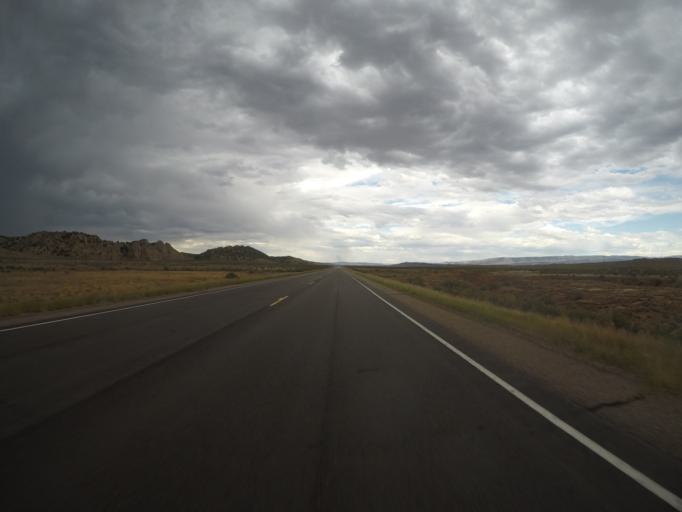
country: US
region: Colorado
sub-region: Rio Blanco County
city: Rangely
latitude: 40.2496
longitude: -108.7580
